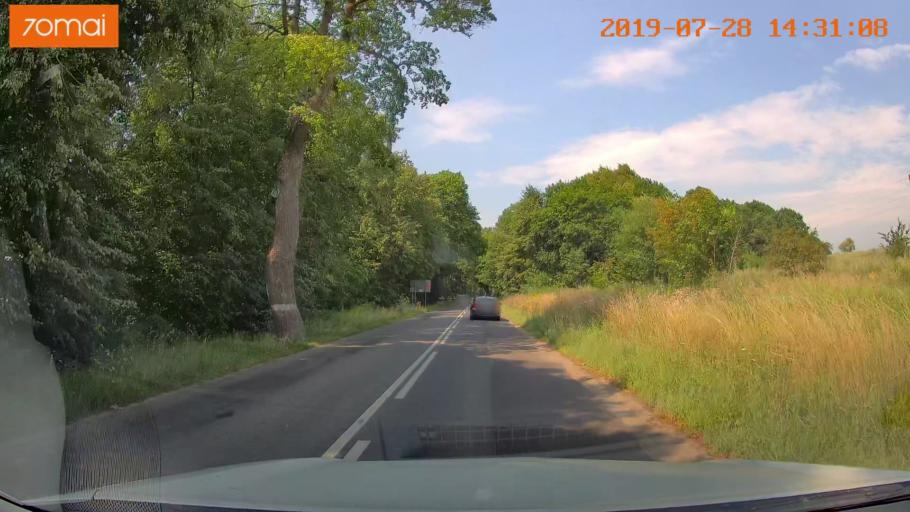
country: RU
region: Kaliningrad
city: Primorsk
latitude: 54.8044
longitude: 20.0539
